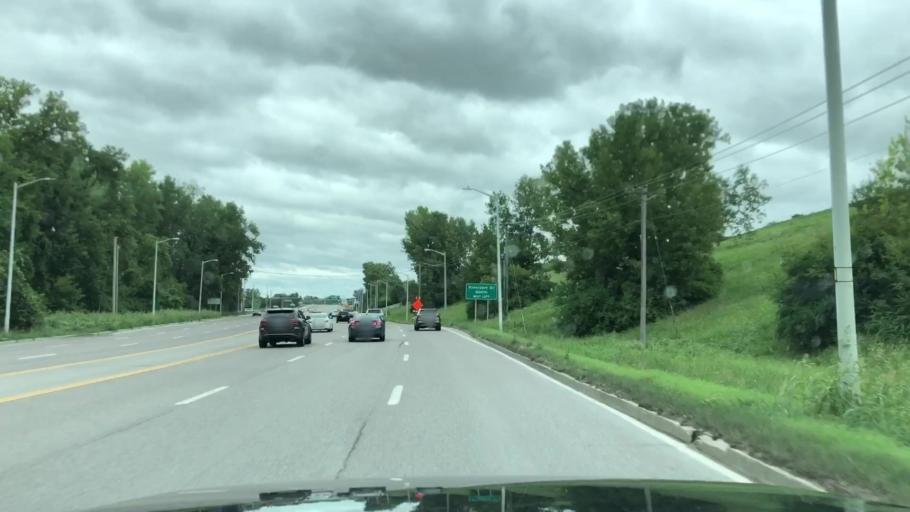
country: US
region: Missouri
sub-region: Saint Charles County
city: Saint Charles
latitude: 38.7460
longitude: -90.4645
